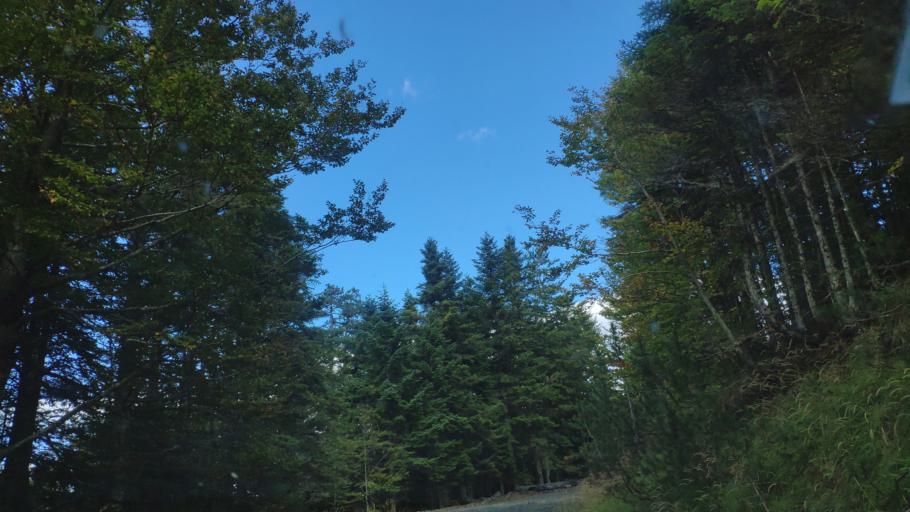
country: AL
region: Korce
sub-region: Rrethi i Devollit
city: Miras
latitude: 40.3371
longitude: 20.8975
